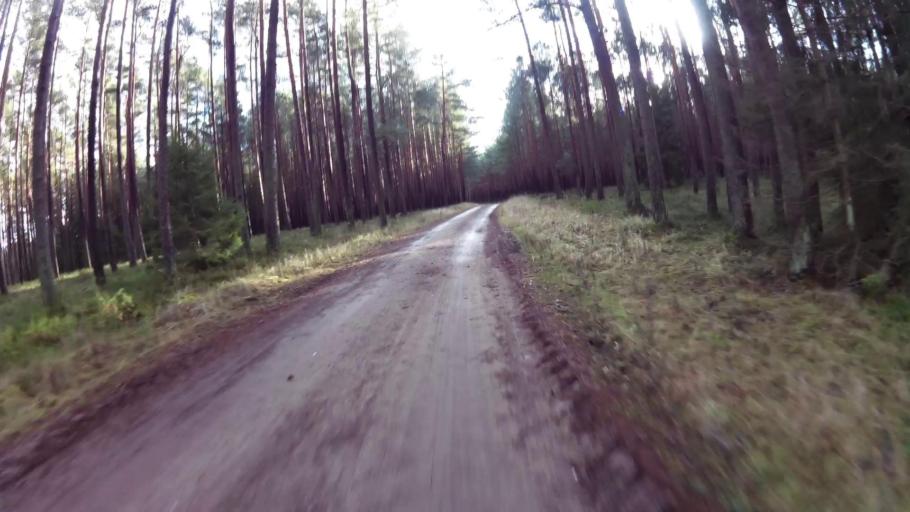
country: PL
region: West Pomeranian Voivodeship
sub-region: Powiat koszalinski
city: Sianow
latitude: 54.1050
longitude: 16.2978
